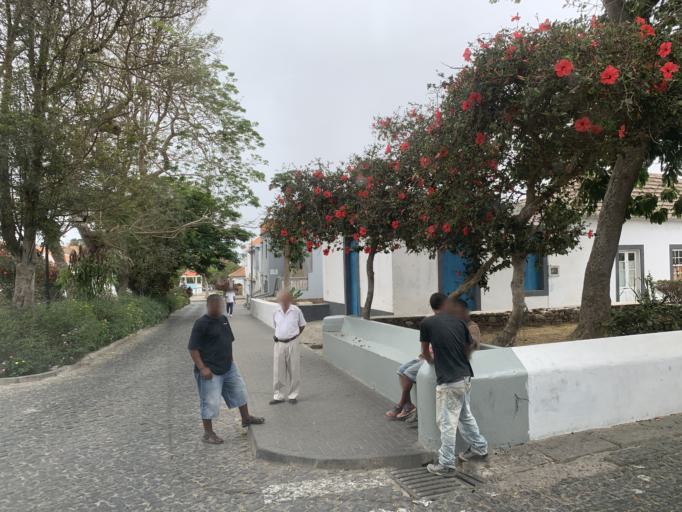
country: CV
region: Brava
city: Vila Nova Sintra
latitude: 14.8708
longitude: -24.6967
